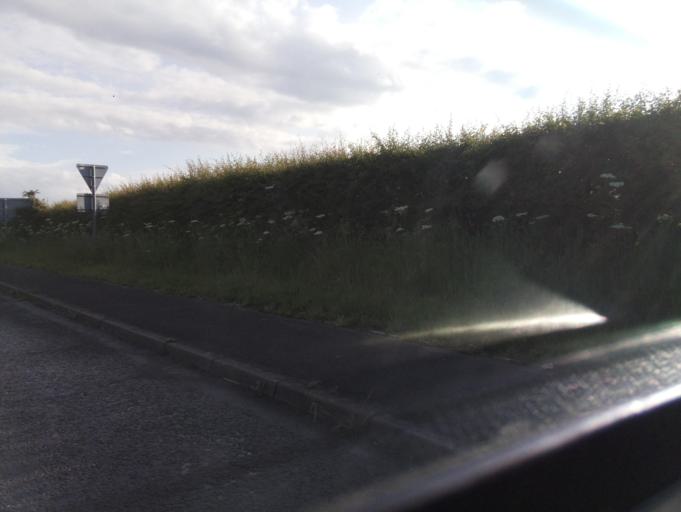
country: GB
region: England
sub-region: Lincolnshire
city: Navenby
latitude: 53.0681
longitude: -0.6358
